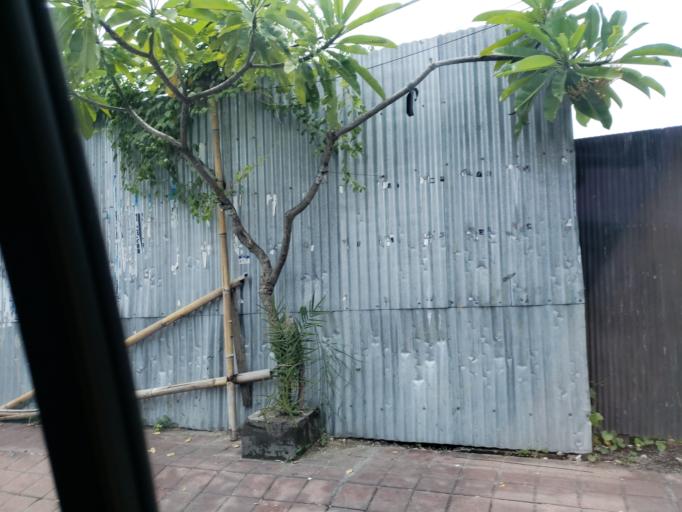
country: ID
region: Bali
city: Kuta
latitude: -8.6788
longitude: 115.1535
